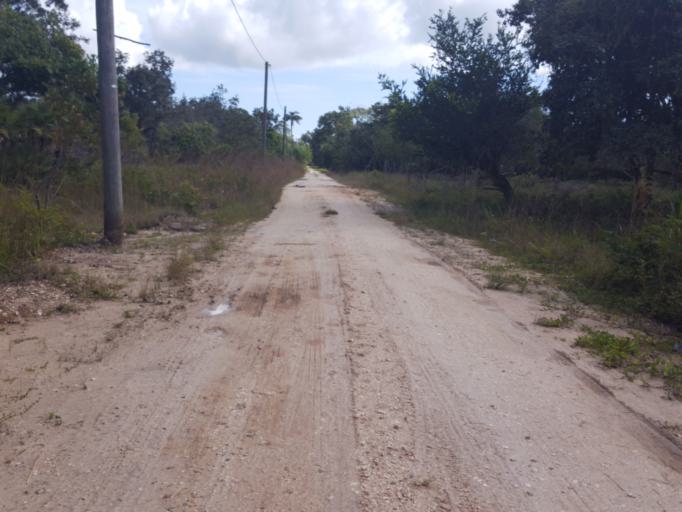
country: BZ
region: Belize
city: Belize City
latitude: 17.5709
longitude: -88.4078
